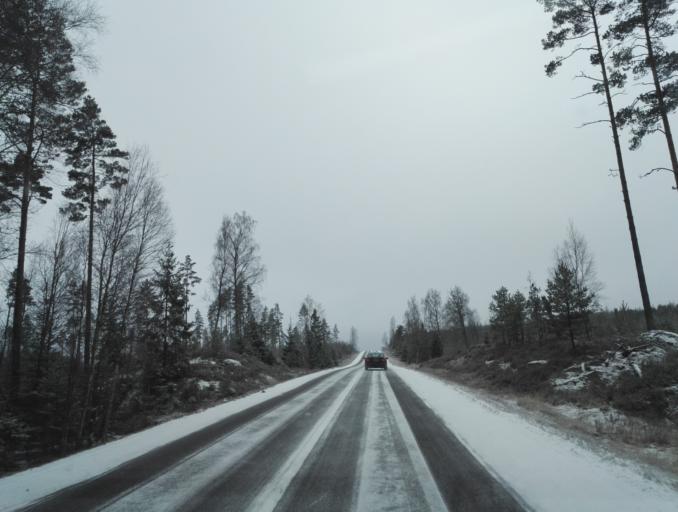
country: SE
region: Kronoberg
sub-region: Lessebo Kommun
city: Lessebo
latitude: 56.7774
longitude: 15.3015
